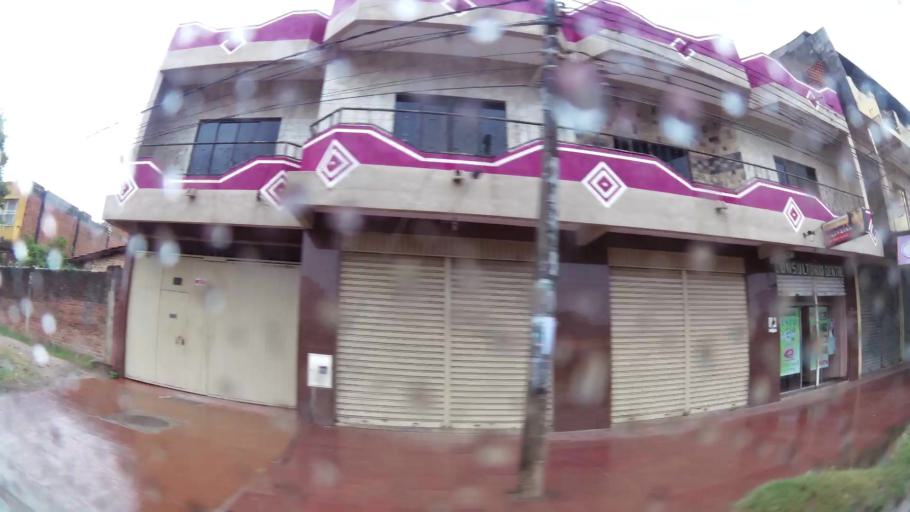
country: BO
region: Santa Cruz
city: Santa Cruz de la Sierra
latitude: -17.8074
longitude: -63.1283
